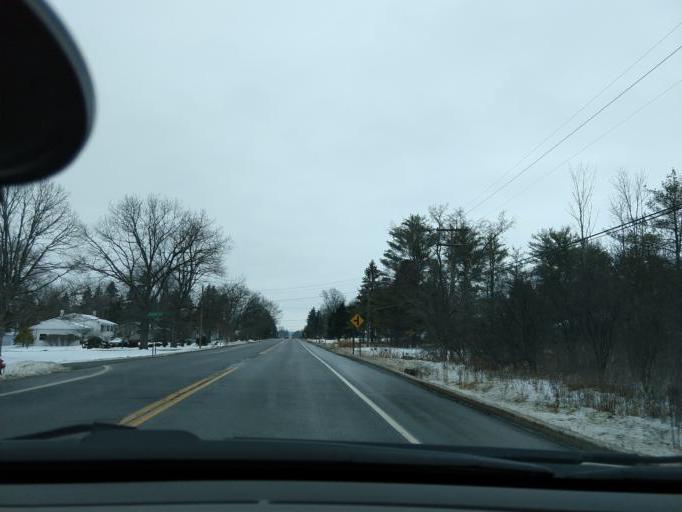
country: US
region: New York
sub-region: Tompkins County
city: Lansing
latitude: 42.5322
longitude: -76.4922
